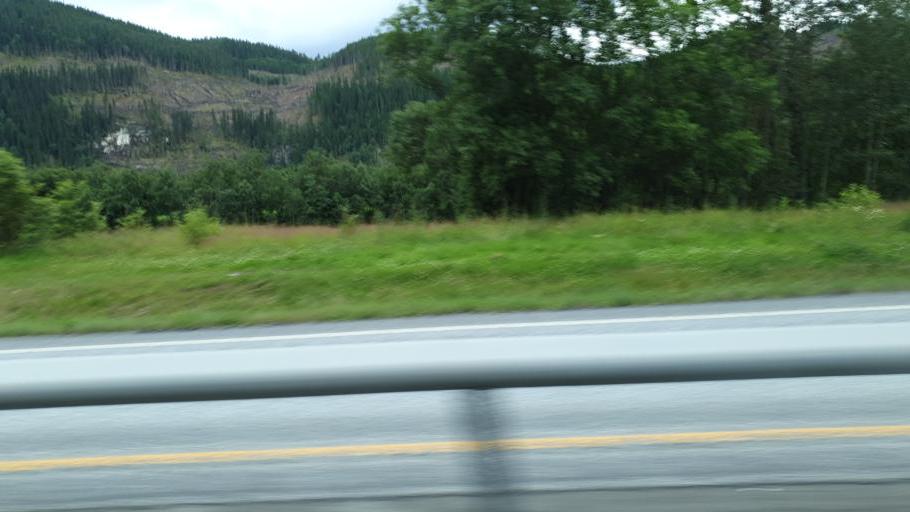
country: NO
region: Sor-Trondelag
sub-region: Midtre Gauldal
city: Storen
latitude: 63.0815
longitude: 10.2560
